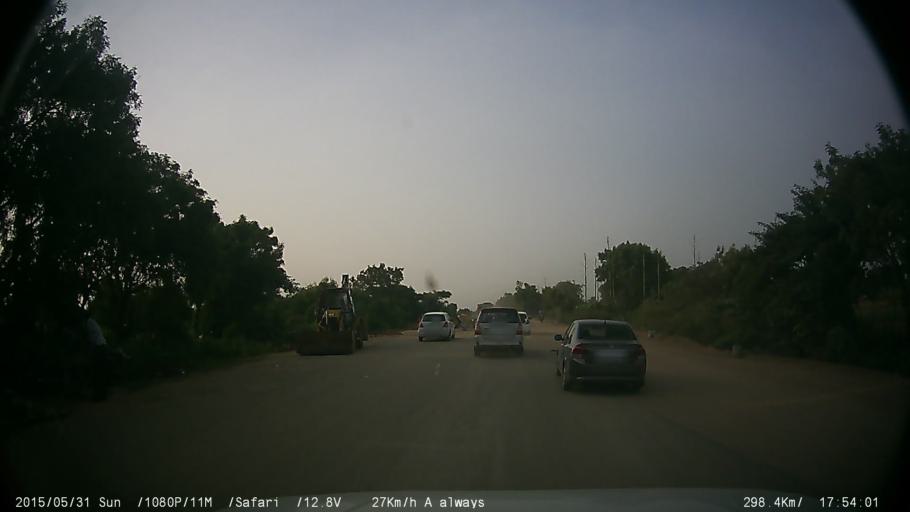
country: IN
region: Karnataka
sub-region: Mysore
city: Nanjangud
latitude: 11.9857
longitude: 76.6692
